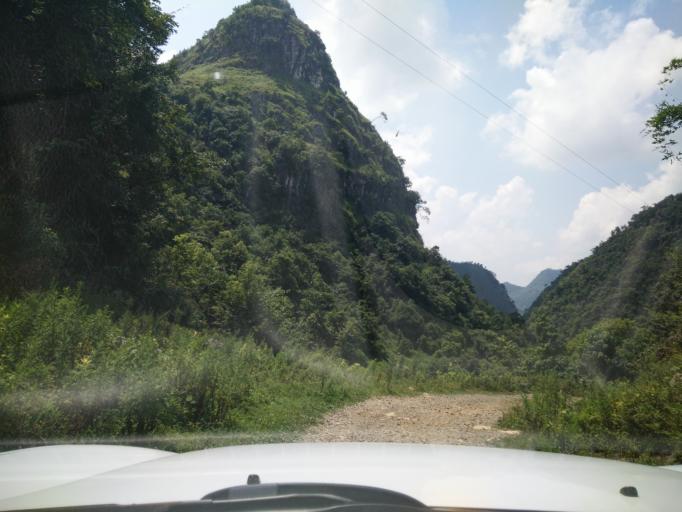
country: CN
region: Guangxi Zhuangzu Zizhiqu
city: Xinzhou
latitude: 25.0168
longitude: 105.7049
